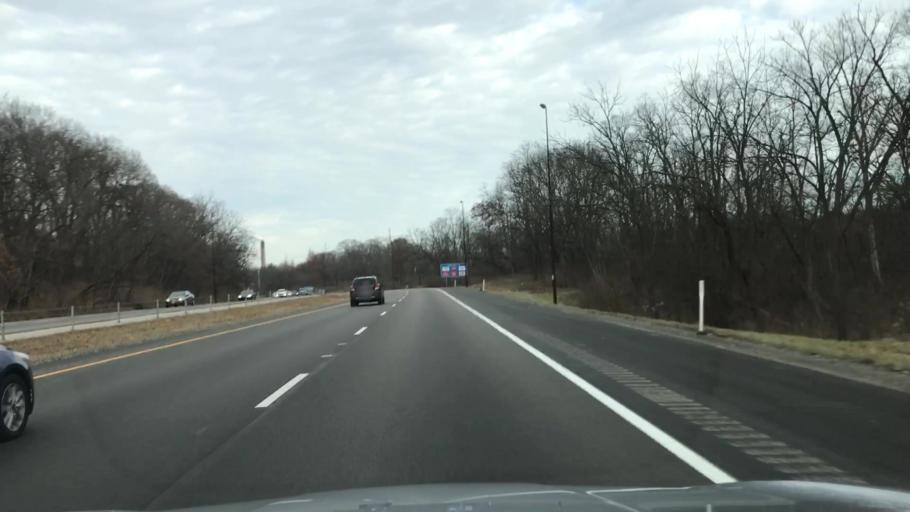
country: US
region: Illinois
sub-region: Sangamon County
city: Southern View
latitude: 39.7456
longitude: -89.6259
